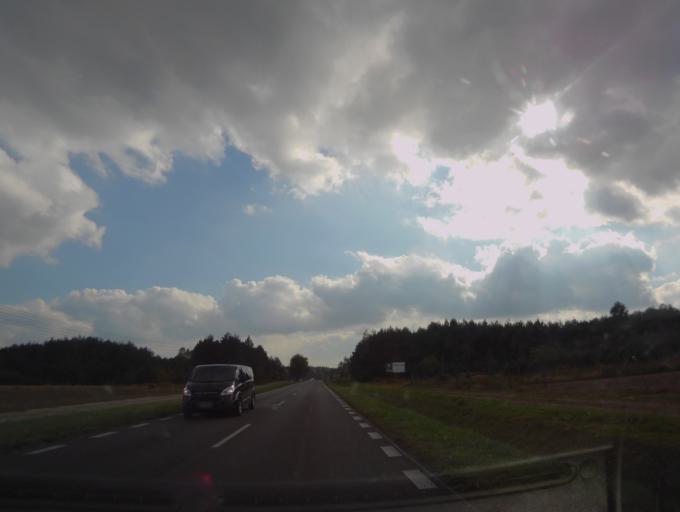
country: PL
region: Lublin Voivodeship
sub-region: Powiat bilgorajski
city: Bilgoraj
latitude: 50.5833
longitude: 22.6845
